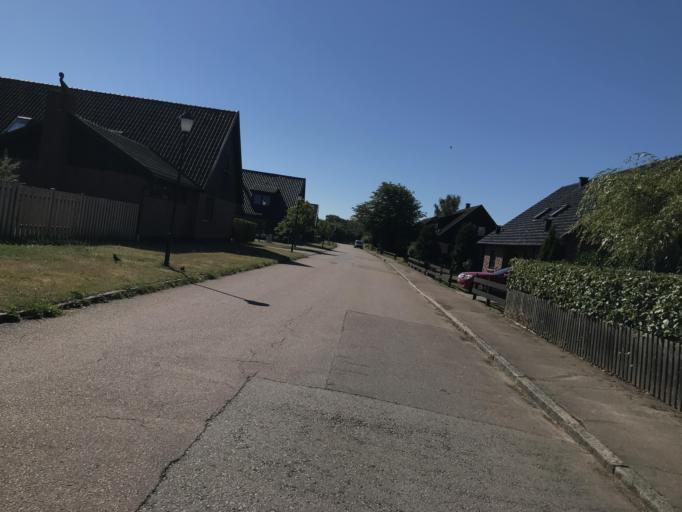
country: SE
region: Skane
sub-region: Landskrona
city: Landskrona
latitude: 55.8867
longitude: 12.8149
